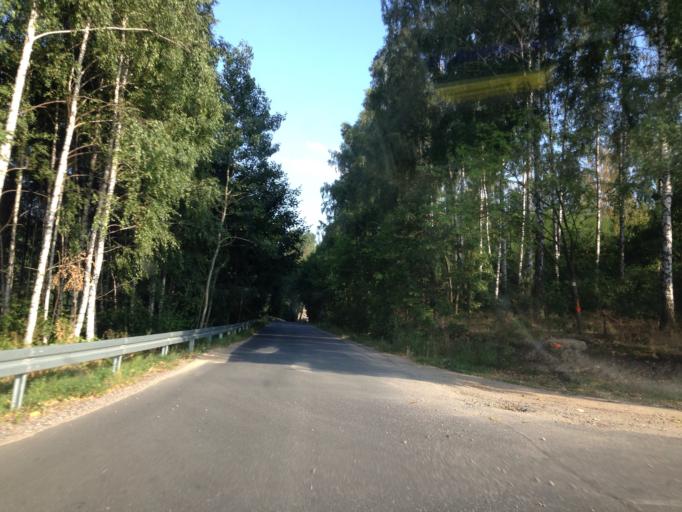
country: PL
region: Warmian-Masurian Voivodeship
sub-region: Powiat nowomiejski
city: Biskupiec
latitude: 53.4192
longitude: 19.3208
